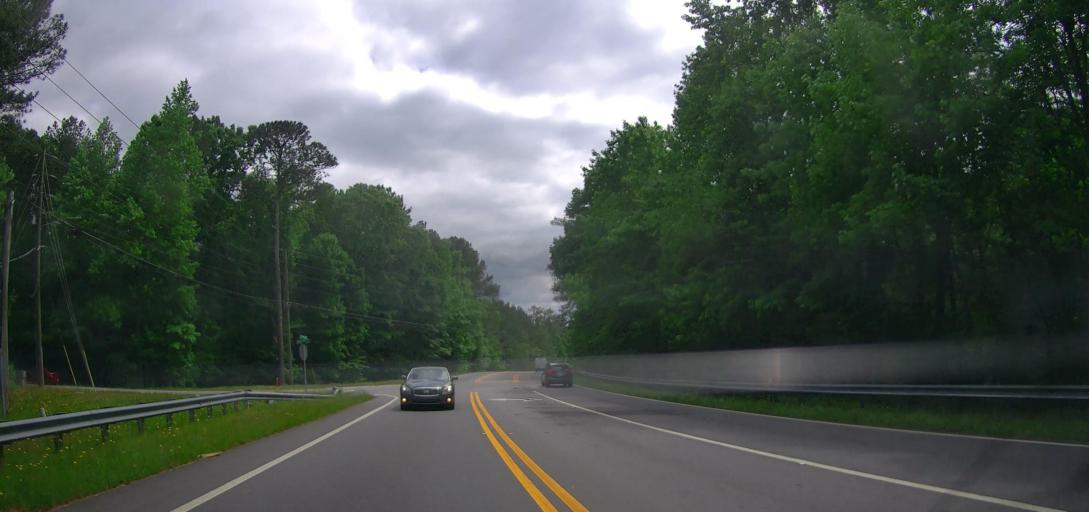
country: US
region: Georgia
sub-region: DeKalb County
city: Pine Mountain
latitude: 33.6056
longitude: -84.0953
